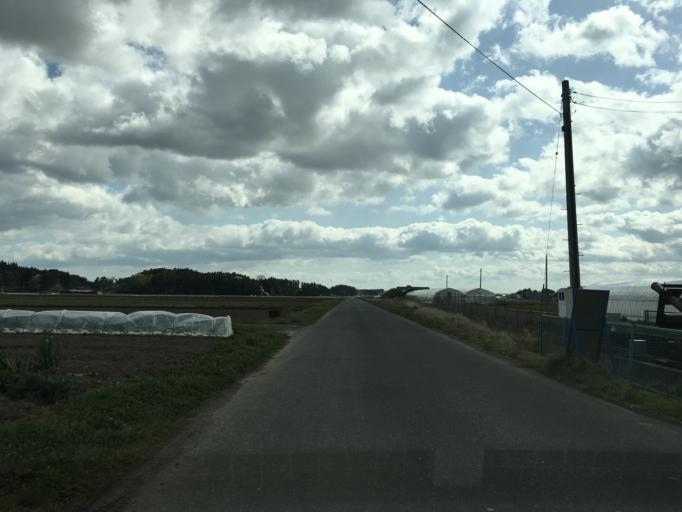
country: JP
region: Iwate
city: Ichinoseki
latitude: 38.7603
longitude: 141.2672
